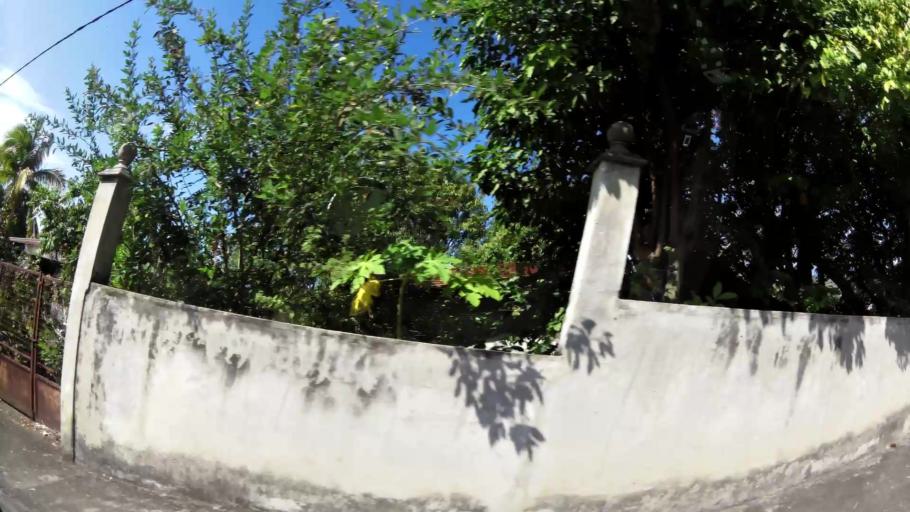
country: GP
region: Guadeloupe
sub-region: Guadeloupe
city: Vieux-Habitants
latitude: 16.0813
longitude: -61.7665
